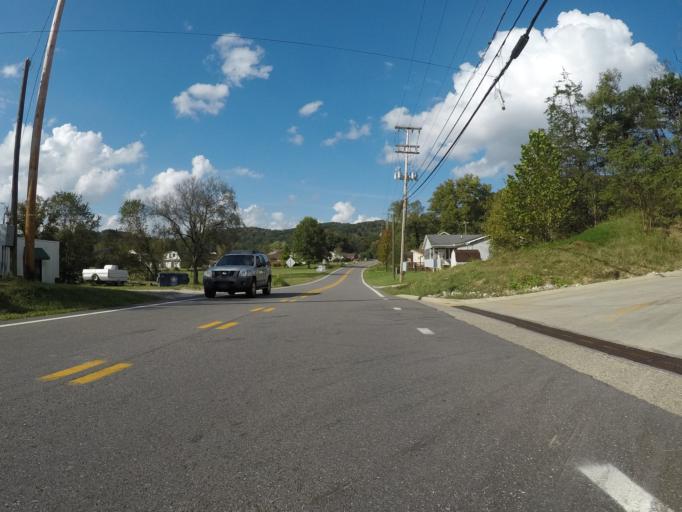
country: US
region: Ohio
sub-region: Lawrence County
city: Burlington
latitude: 38.3553
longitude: -82.5047
